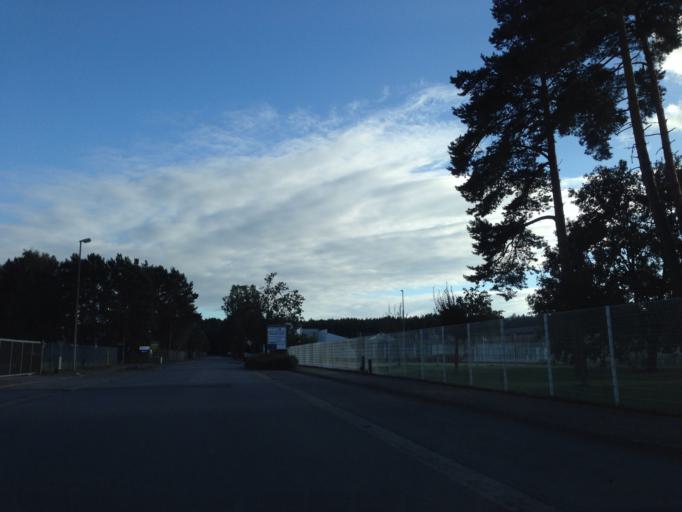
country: DE
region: Lower Saxony
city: Wendisch Evern
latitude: 53.2412
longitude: 10.4786
